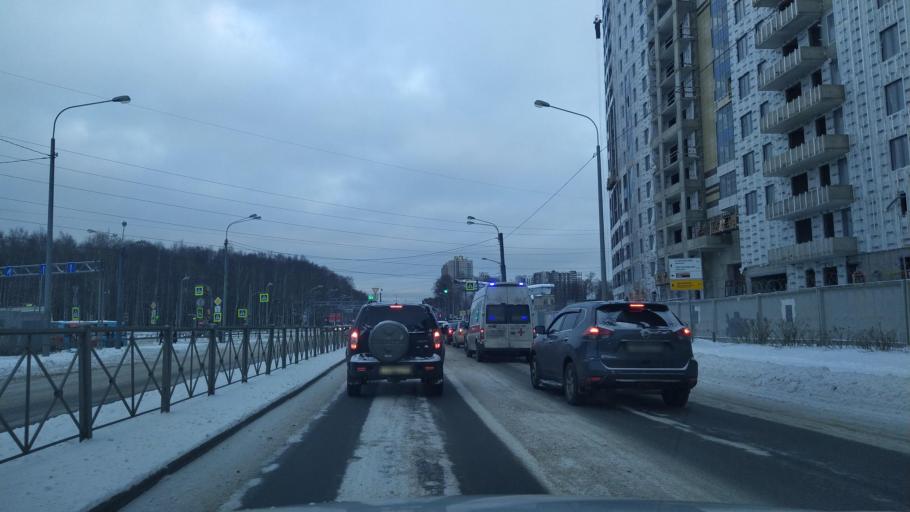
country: RU
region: Leningrad
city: Udel'naya
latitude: 60.0023
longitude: 30.3096
